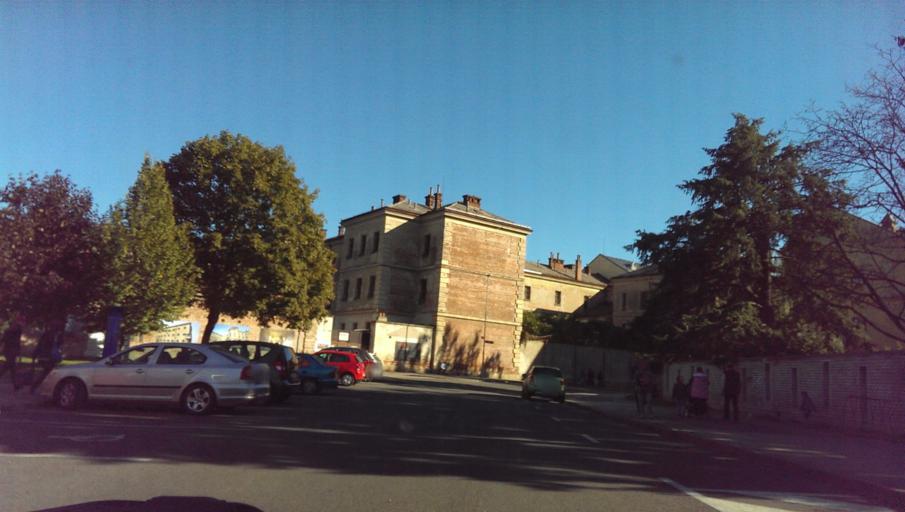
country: CZ
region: Zlin
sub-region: Okres Uherske Hradiste
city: Uherske Hradiste
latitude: 49.0695
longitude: 17.4643
